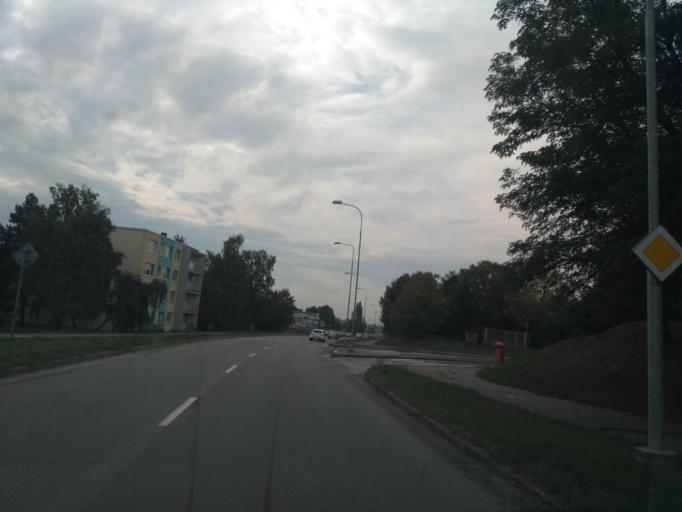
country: SK
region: Kosicky
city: Kosice
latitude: 48.7078
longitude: 21.2293
